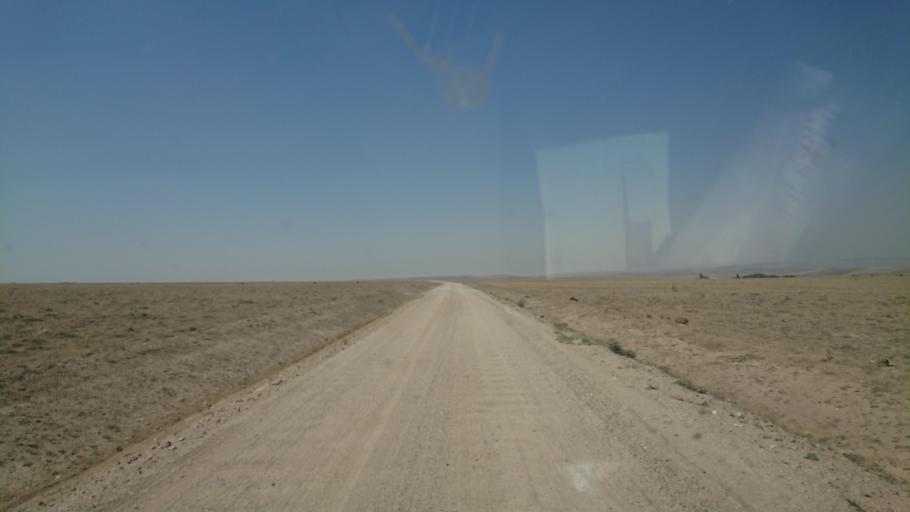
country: TR
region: Aksaray
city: Agacoren
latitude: 38.7484
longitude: 33.9064
